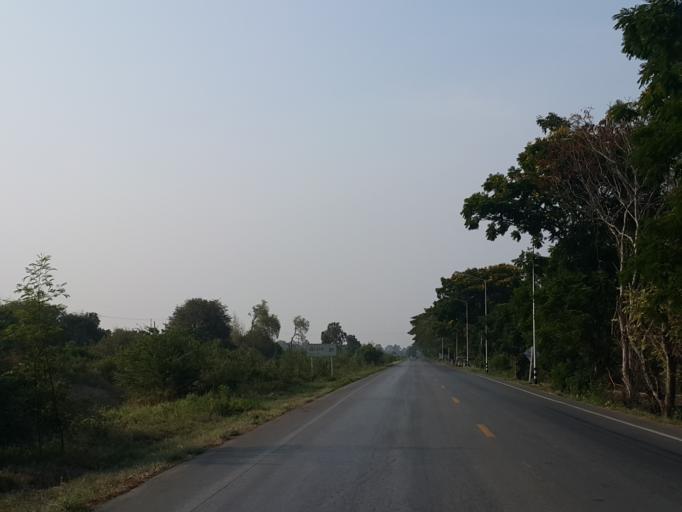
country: TH
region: Chai Nat
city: Sankhaburi
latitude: 15.0237
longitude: 100.1447
